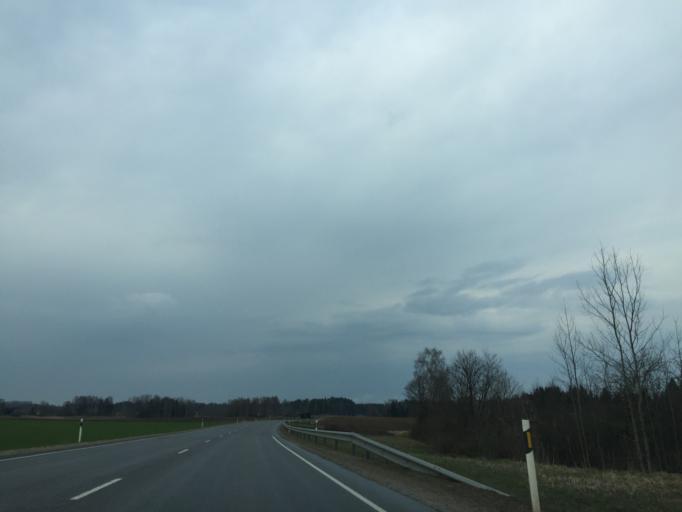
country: EE
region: Tartu
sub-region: UElenurme vald
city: Ulenurme
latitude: 58.0872
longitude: 26.7339
